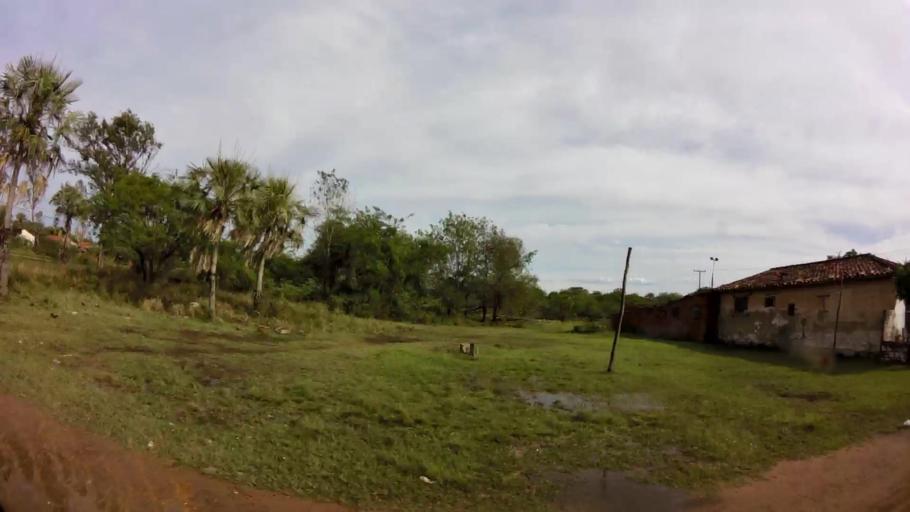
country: PY
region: Central
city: Limpio
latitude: -25.1748
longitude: -57.4948
